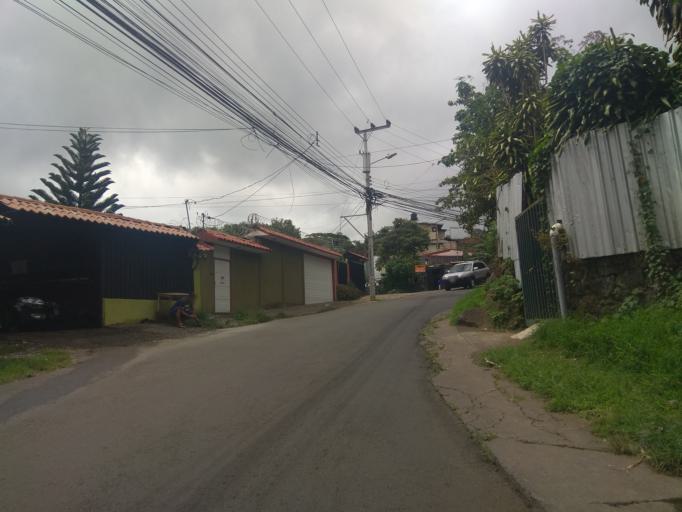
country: CR
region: Heredia
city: San Josecito
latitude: 10.0305
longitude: -84.1079
